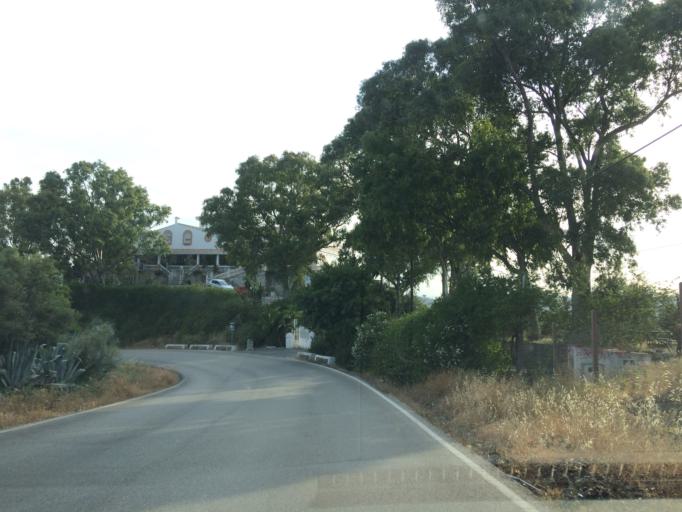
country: ES
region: Andalusia
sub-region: Provincia de Malaga
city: Malaga
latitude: 36.7458
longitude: -4.4103
